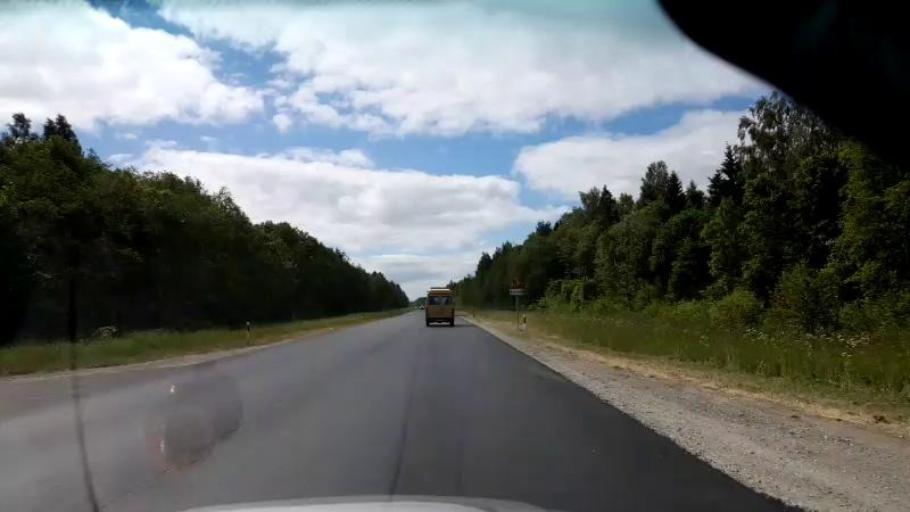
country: LV
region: Salacgrivas
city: Ainazi
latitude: 57.9369
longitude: 24.4294
